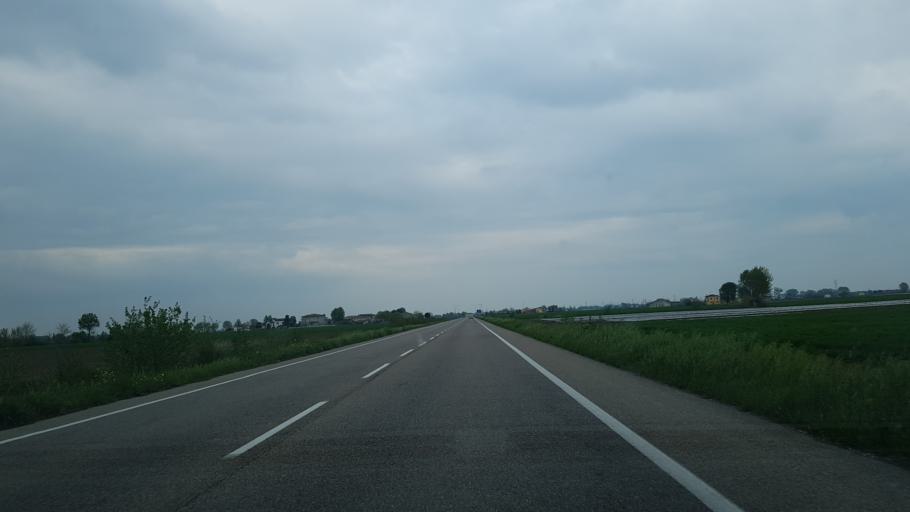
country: IT
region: Veneto
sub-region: Provincia di Rovigo
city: Melara
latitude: 45.0789
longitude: 11.1948
